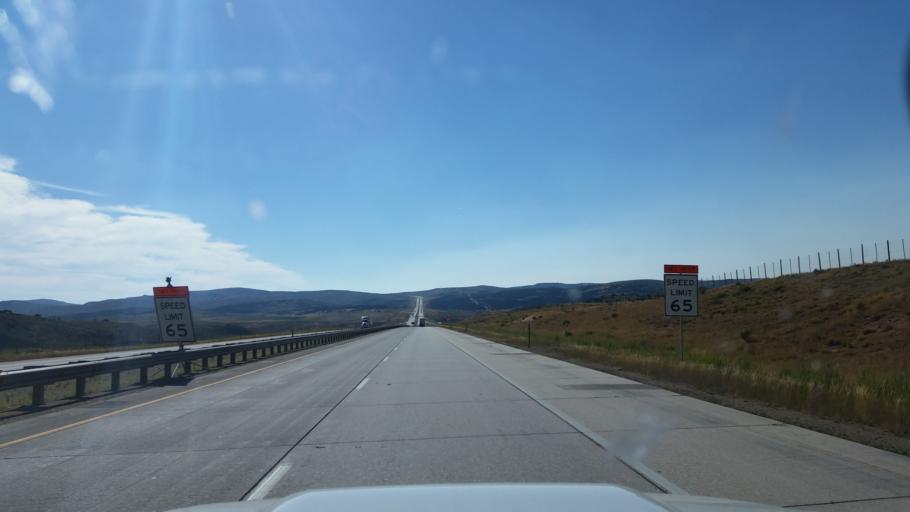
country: US
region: Wyoming
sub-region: Uinta County
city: Mountain View
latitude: 41.2984
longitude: -110.6156
